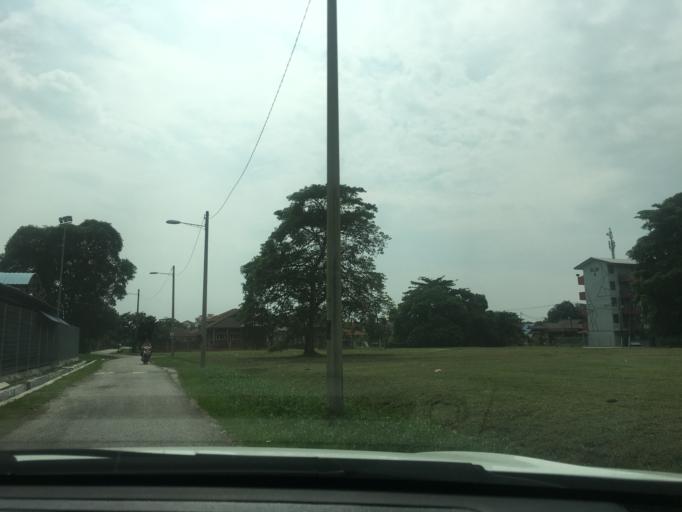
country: MY
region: Selangor
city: Klang
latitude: 3.0501
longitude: 101.4384
